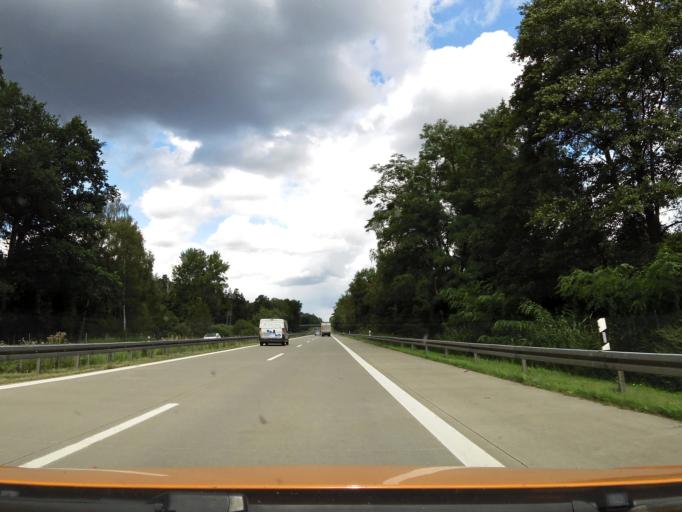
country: DE
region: Brandenburg
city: Althuttendorf
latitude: 53.0329
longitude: 13.8315
